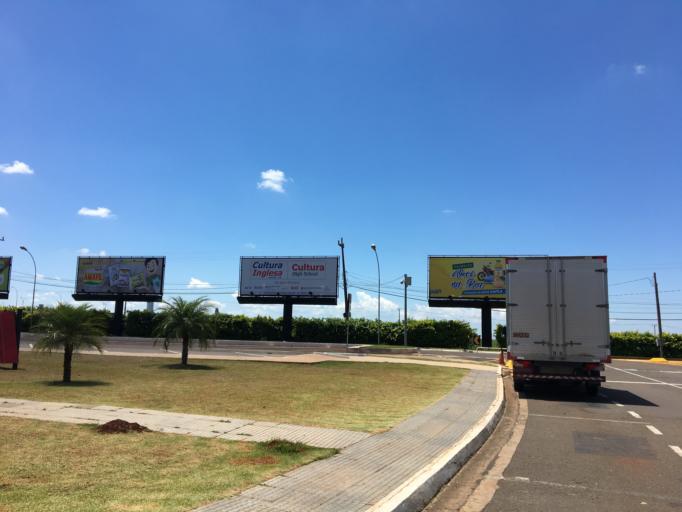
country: BR
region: Parana
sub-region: Paicandu
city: Paicandu
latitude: -23.4800
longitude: -52.0124
